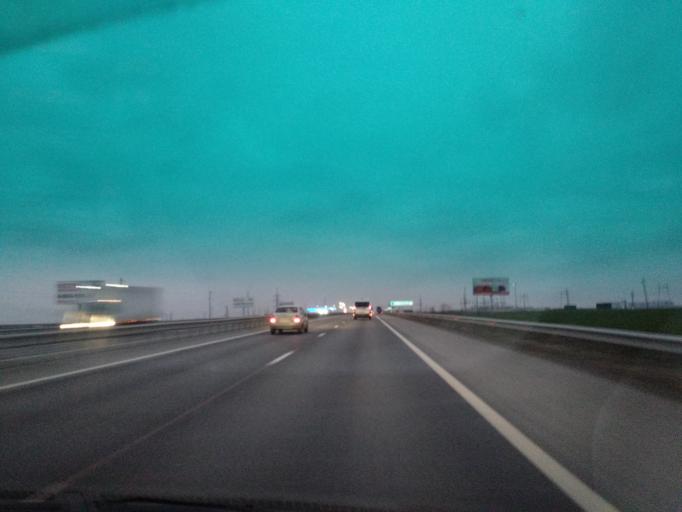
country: RU
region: Adygeya
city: Adygeysk
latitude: 44.8623
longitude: 39.1940
